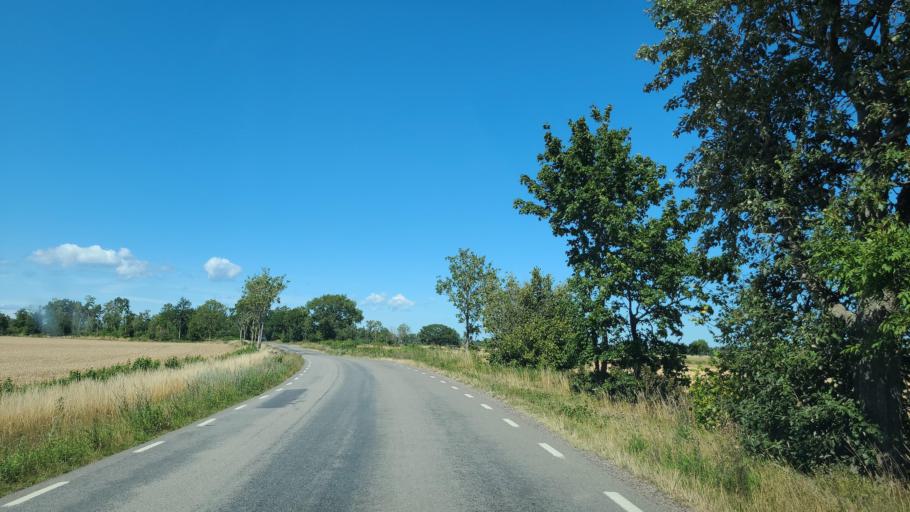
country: SE
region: Kalmar
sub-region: Borgholms Kommun
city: Borgholm
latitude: 56.7603
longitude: 16.7376
